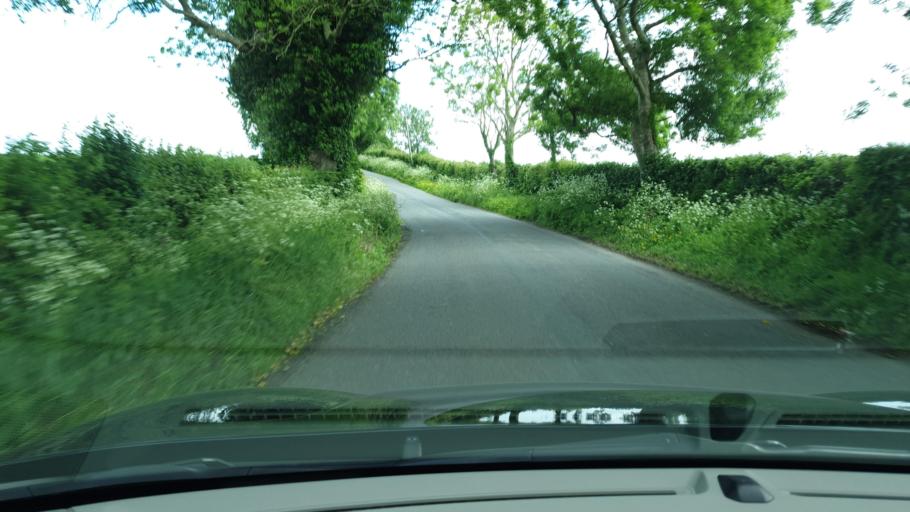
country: IE
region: Leinster
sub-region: An Mhi
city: Navan
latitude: 53.7942
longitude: -6.6888
